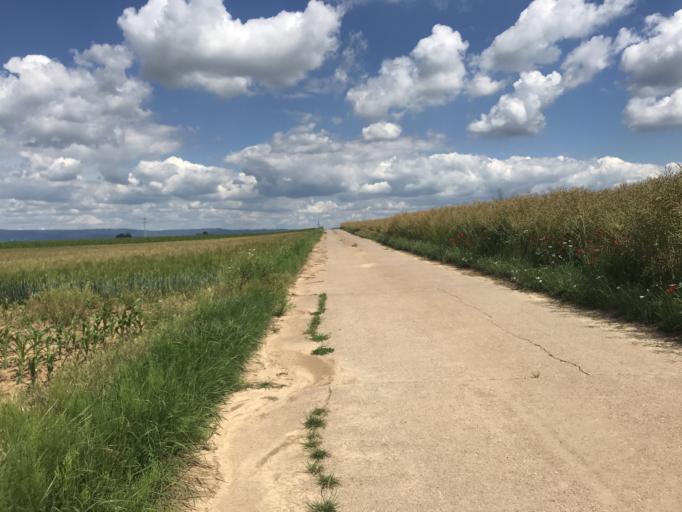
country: DE
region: Rheinland-Pfalz
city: Essenheim
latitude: 49.9401
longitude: 8.1404
